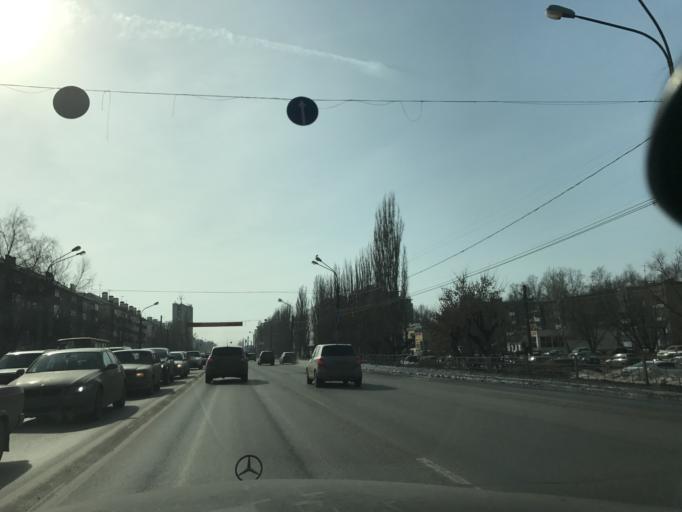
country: RU
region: Nizjnij Novgorod
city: Nizhniy Novgorod
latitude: 56.2809
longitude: 43.9247
